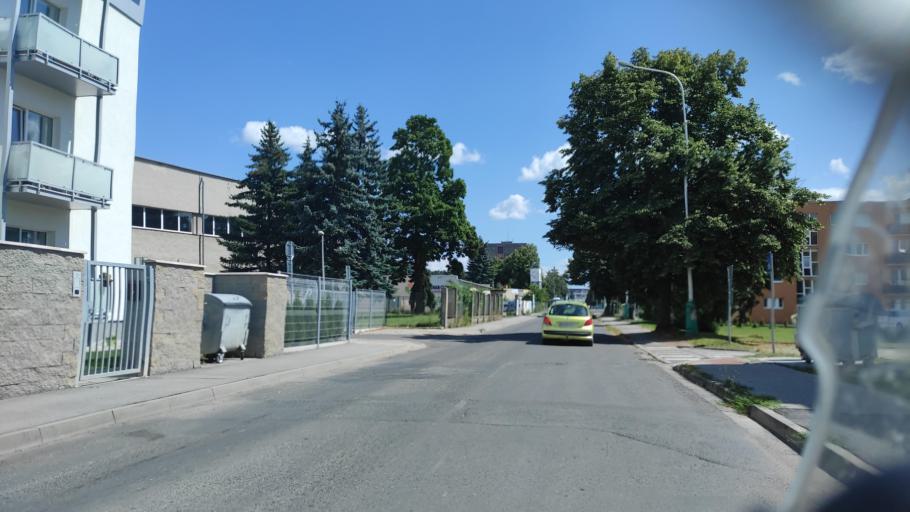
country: SK
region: Zilinsky
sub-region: Okres Liptovsky Mikulas
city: Liptovsky Mikulas
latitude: 49.0833
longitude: 19.6219
